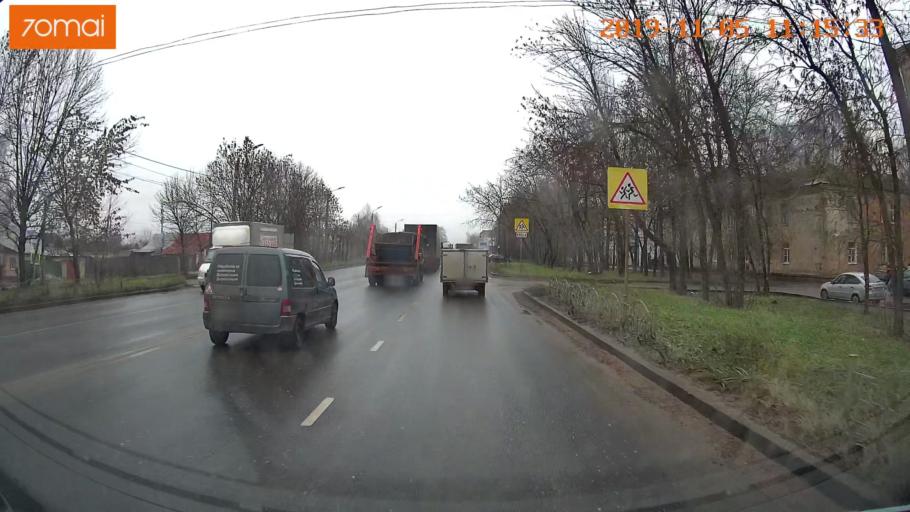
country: RU
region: Ivanovo
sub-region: Gorod Ivanovo
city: Ivanovo
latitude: 56.9782
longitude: 40.9541
